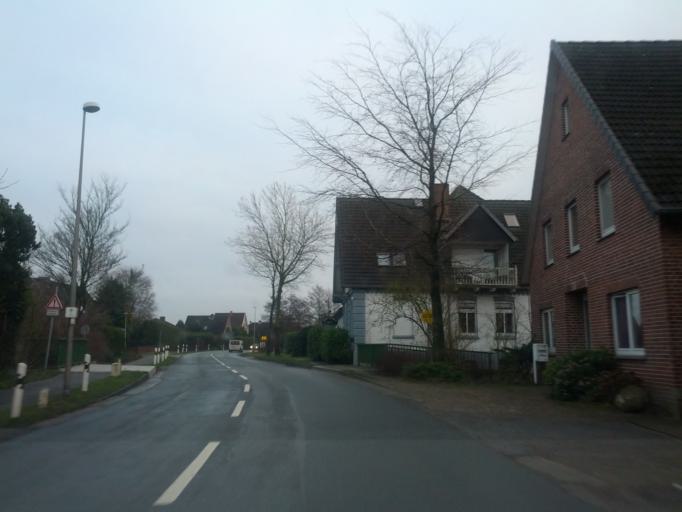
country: DE
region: Lower Saxony
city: Jork
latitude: 53.5256
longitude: 9.7081
